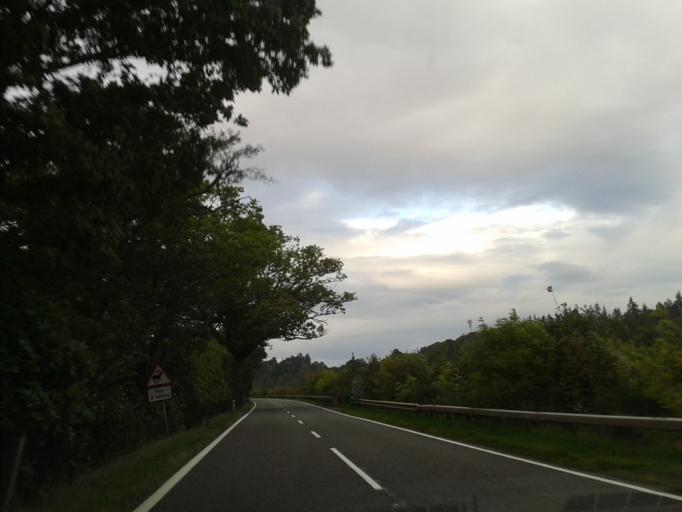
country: GB
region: Scotland
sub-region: Highland
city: Inverness
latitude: 57.4216
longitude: -4.3220
